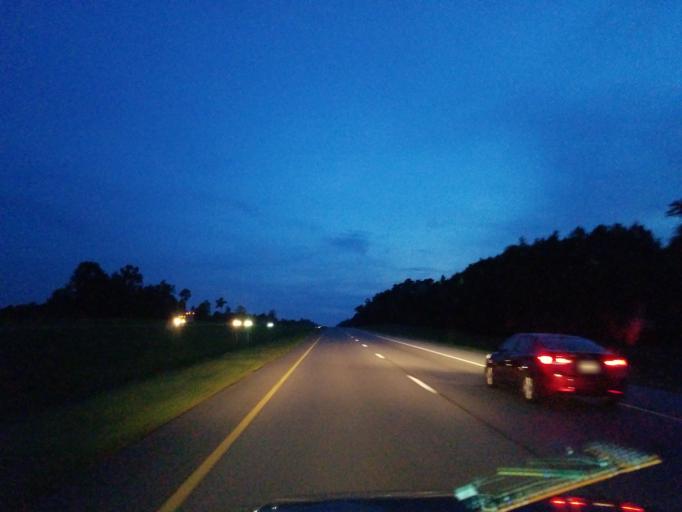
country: US
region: Mississippi
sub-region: Jones County
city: Ellisville
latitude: 31.5742
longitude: -89.2474
